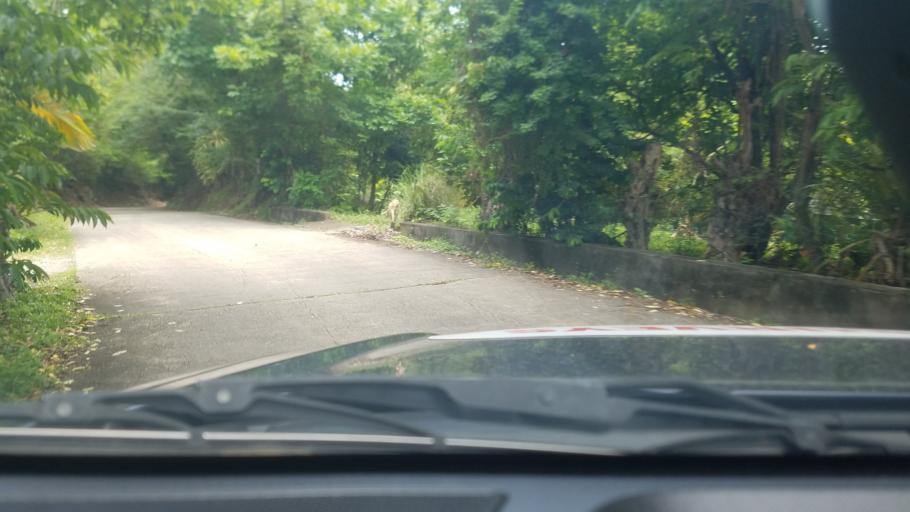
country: LC
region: Soufriere
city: Soufriere
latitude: 13.8388
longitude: -61.0612
